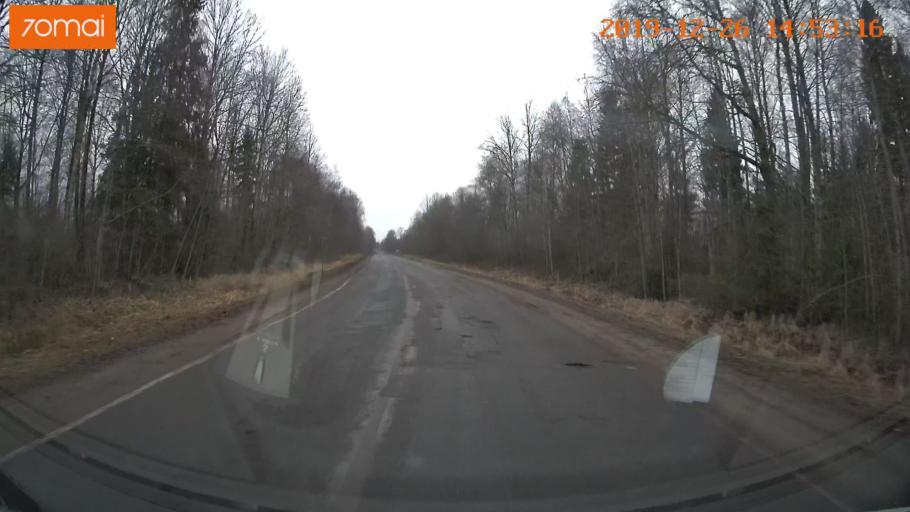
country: RU
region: Jaroslavl
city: Rybinsk
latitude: 58.3165
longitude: 38.8905
